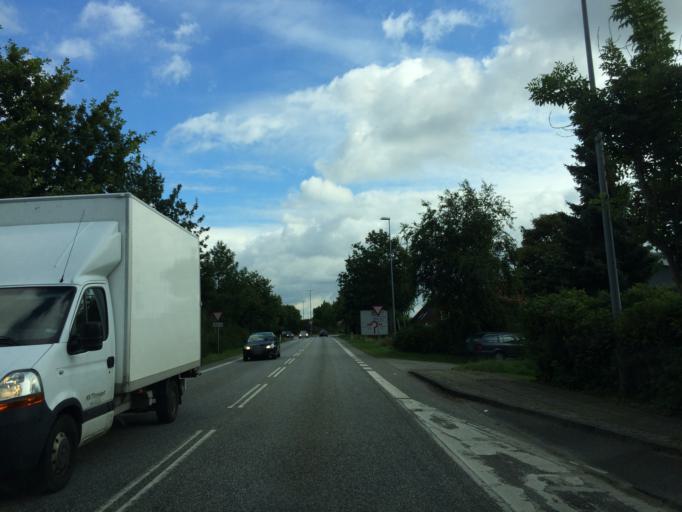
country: DK
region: Central Jutland
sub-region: Holstebro Kommune
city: Holstebro
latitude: 56.3647
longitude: 8.6970
